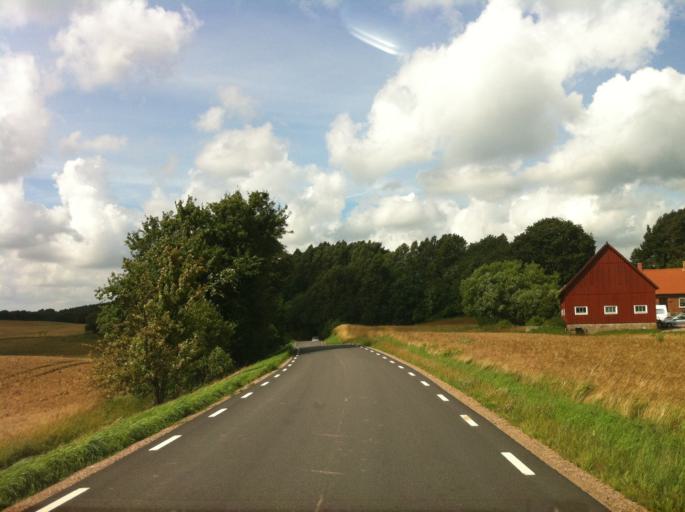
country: SE
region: Skane
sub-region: Trelleborgs Kommun
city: Anderslov
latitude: 55.4552
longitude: 13.3701
